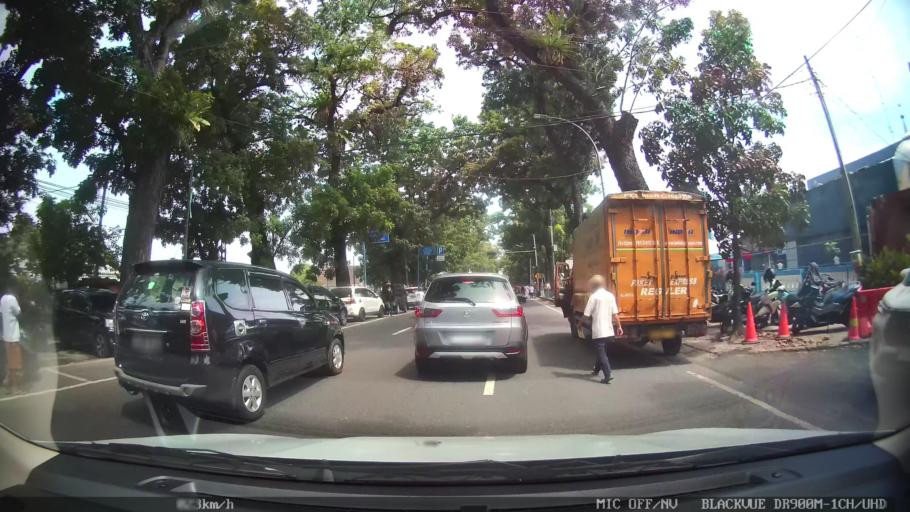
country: ID
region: North Sumatra
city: Medan
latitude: 3.5972
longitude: 98.6749
